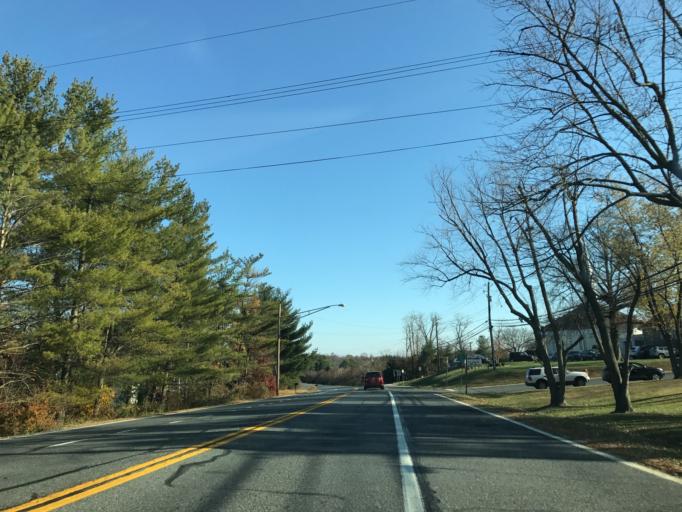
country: US
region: Maryland
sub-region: Howard County
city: Columbia
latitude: 39.2258
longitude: -76.8038
